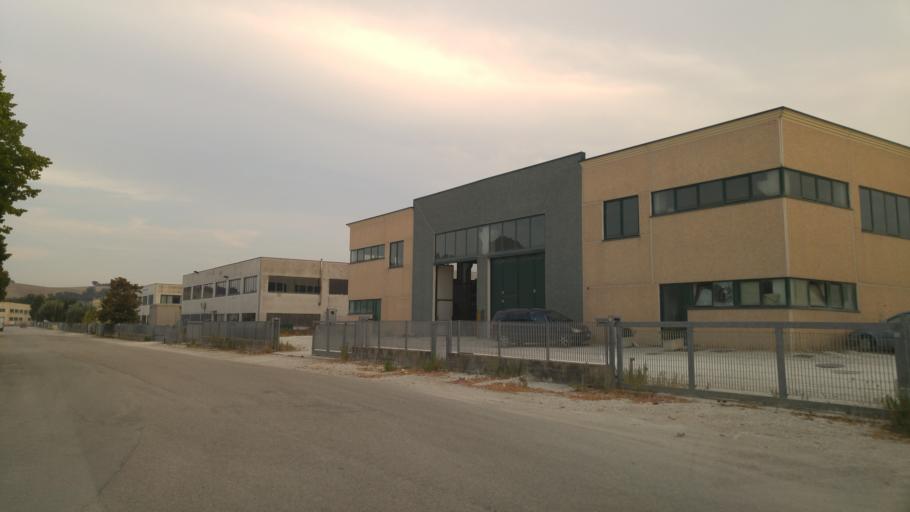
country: IT
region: The Marches
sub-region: Provincia di Pesaro e Urbino
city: Bellocchi
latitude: 43.7857
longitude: 13.0027
